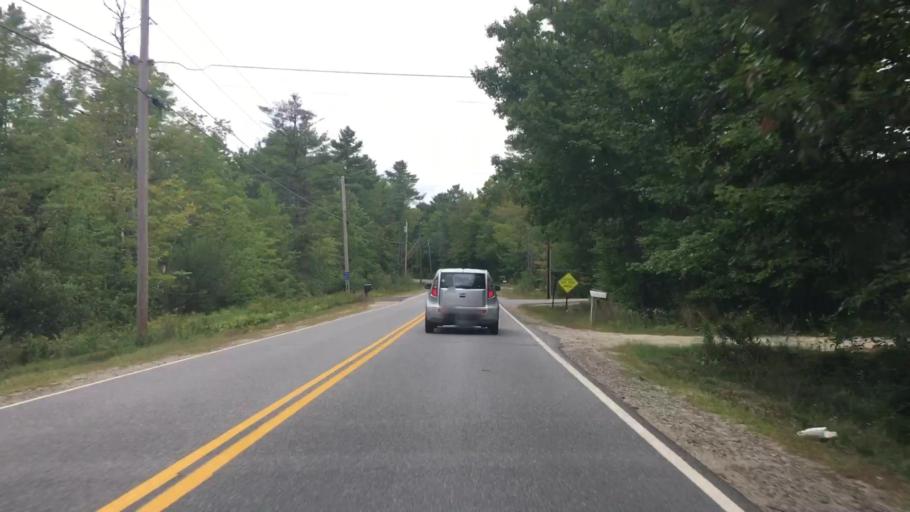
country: US
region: Maine
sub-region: Cumberland County
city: Cumberland Center
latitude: 43.8709
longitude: -70.2311
